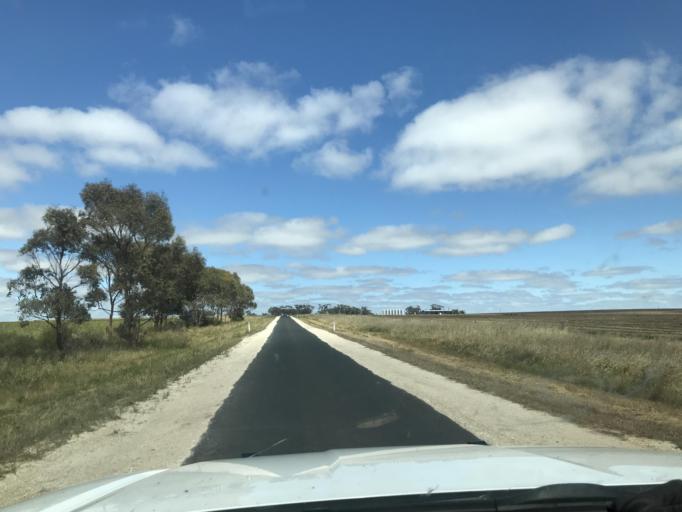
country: AU
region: South Australia
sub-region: Tatiara
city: Bordertown
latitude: -36.3060
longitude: 141.0864
